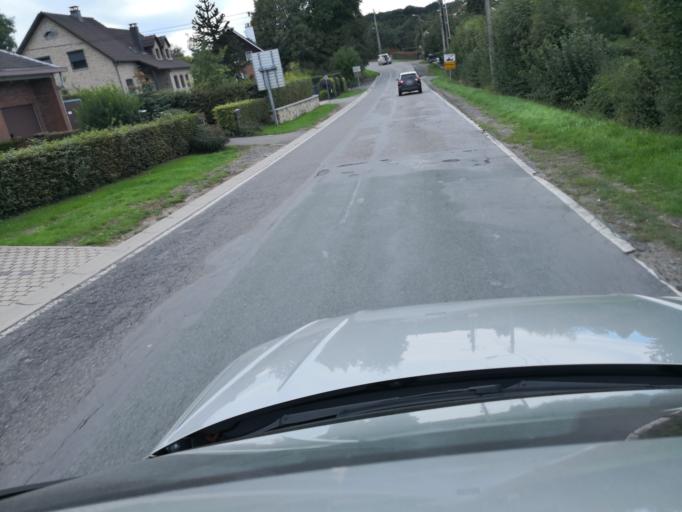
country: BE
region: Wallonia
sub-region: Province de Liege
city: Verviers
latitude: 50.5579
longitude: 5.8960
